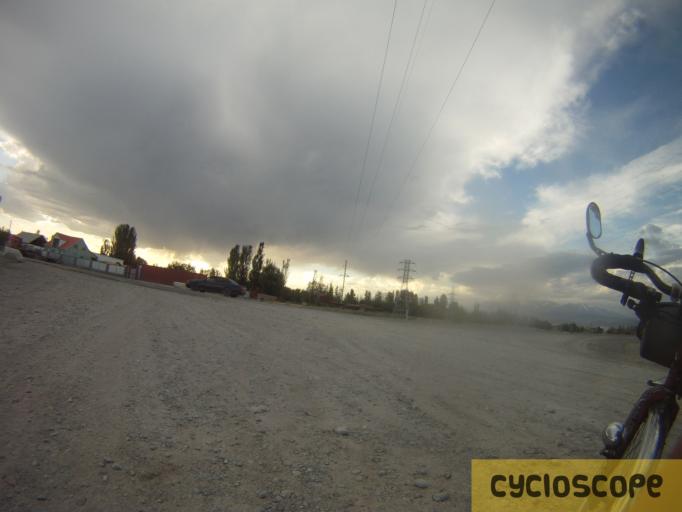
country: KZ
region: Almaty Oblysy
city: Zharkent
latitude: 44.2187
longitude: 80.2218
